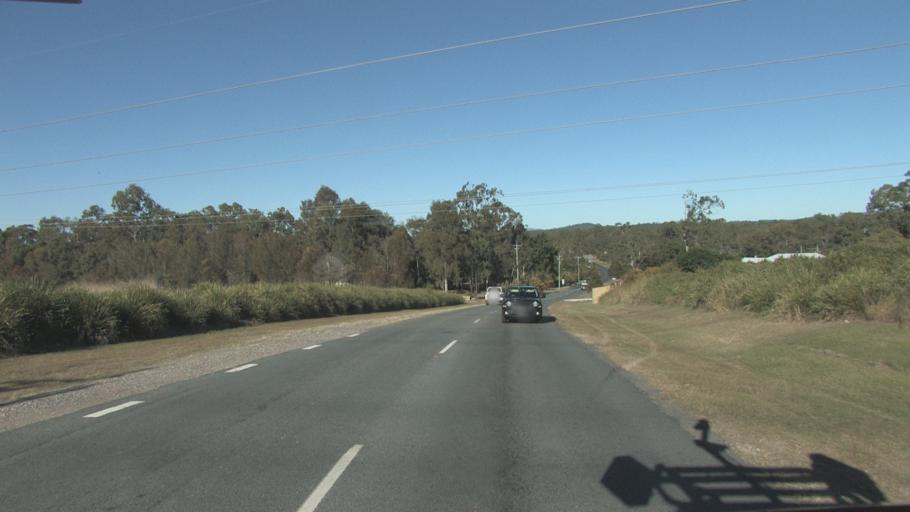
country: AU
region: Queensland
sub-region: Logan
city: North Maclean
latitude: -27.7383
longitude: 152.9699
